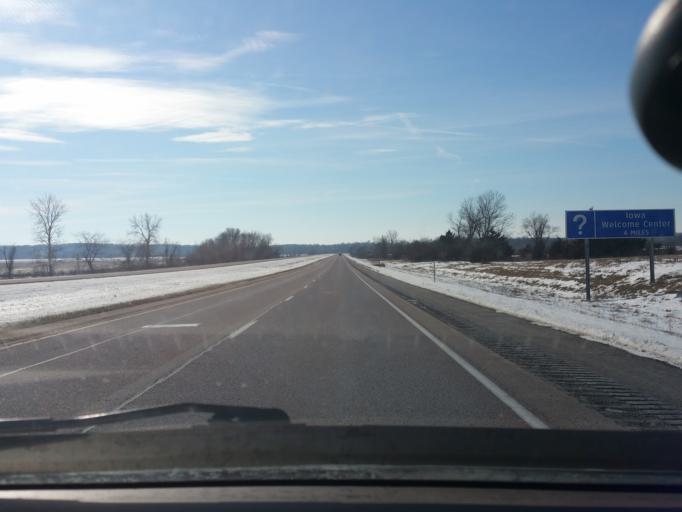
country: US
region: Iowa
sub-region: Decatur County
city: Lamoni
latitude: 40.6803
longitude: -93.8482
